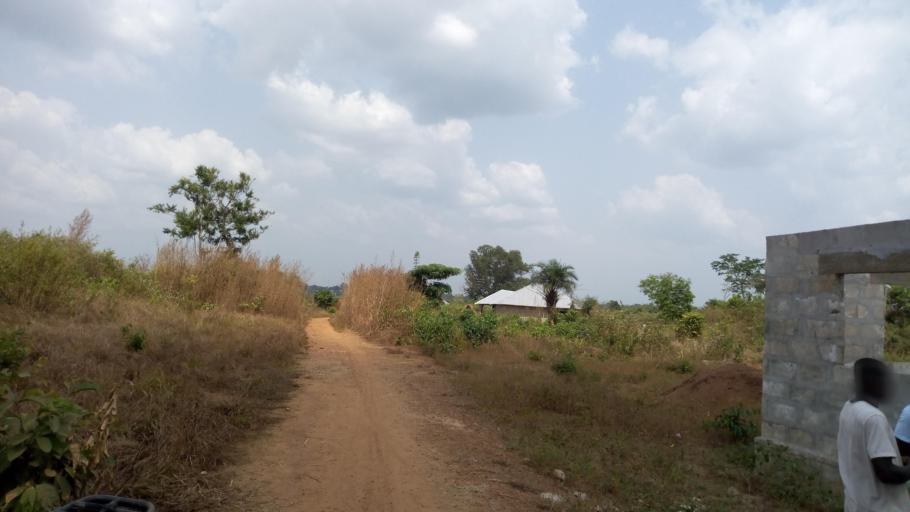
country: SL
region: Southern Province
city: Mogbwemo
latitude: 7.7922
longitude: -12.3065
